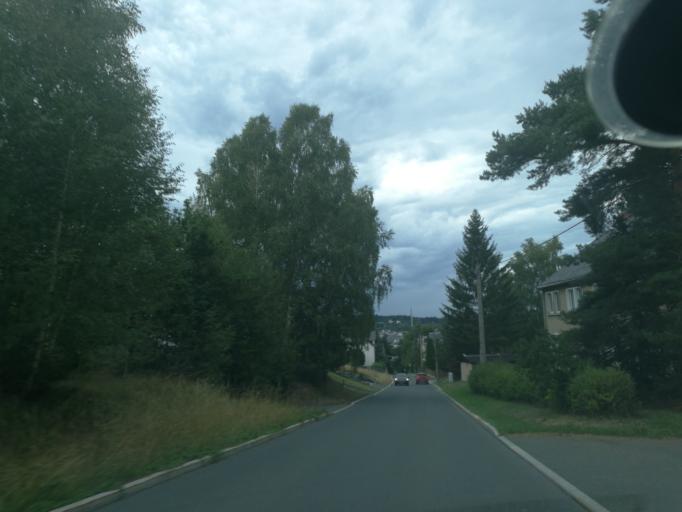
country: DE
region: Saxony
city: Adorf
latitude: 50.3145
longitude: 12.2650
